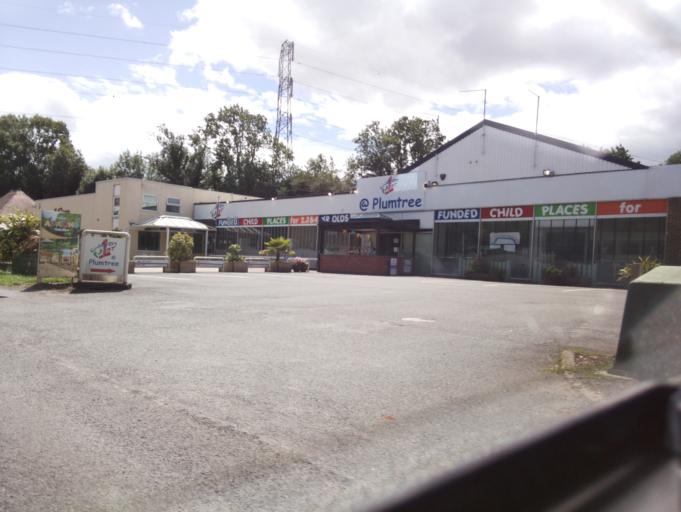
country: GB
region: England
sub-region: Nottinghamshire
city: Cotgrave
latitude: 52.8868
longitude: -1.0867
